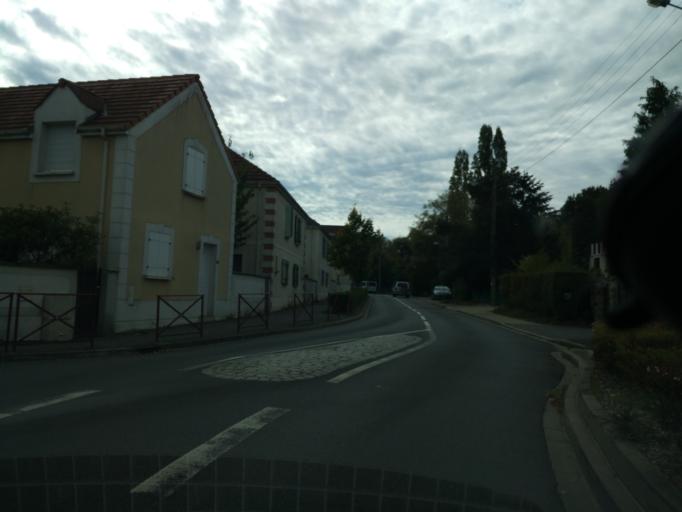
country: FR
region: Ile-de-France
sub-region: Departement de l'Essonne
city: Les Molieres
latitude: 48.6751
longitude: 2.0705
